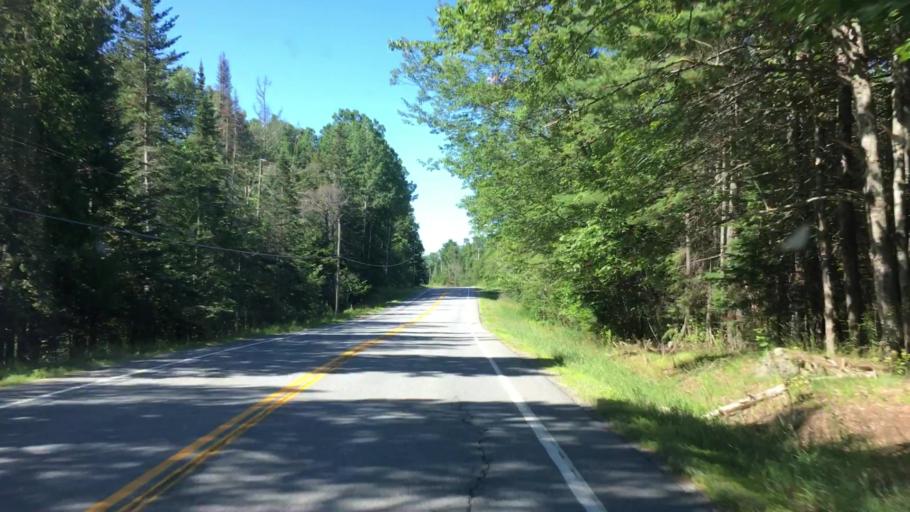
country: US
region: Maine
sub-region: Hancock County
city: Dedham
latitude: 44.6877
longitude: -68.6620
